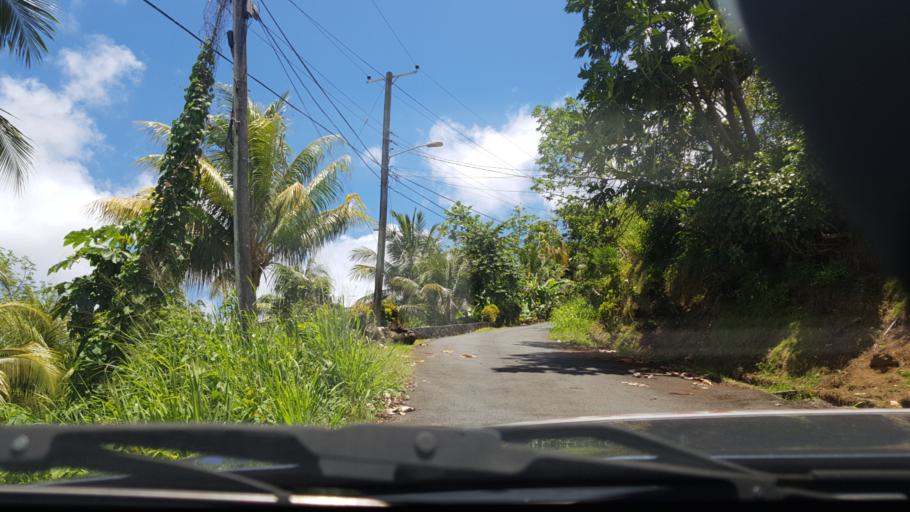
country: LC
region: Anse-la-Raye
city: Anse La Raye
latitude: 13.9552
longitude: -61.0001
